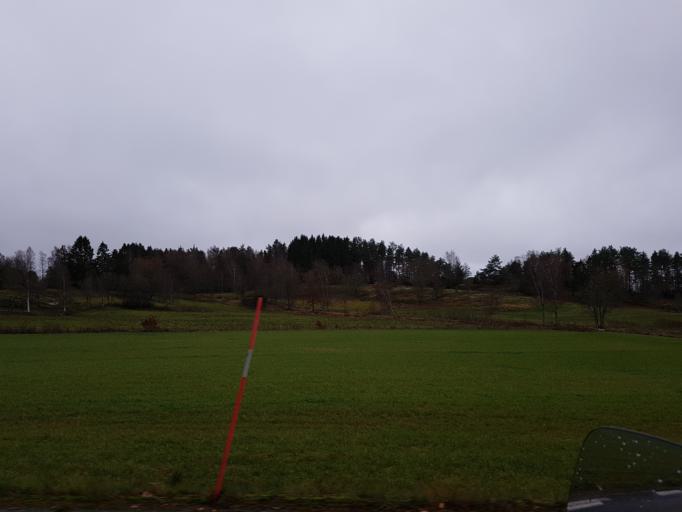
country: SE
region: Vaestra Goetaland
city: Svanesund
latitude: 58.1573
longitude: 11.7860
